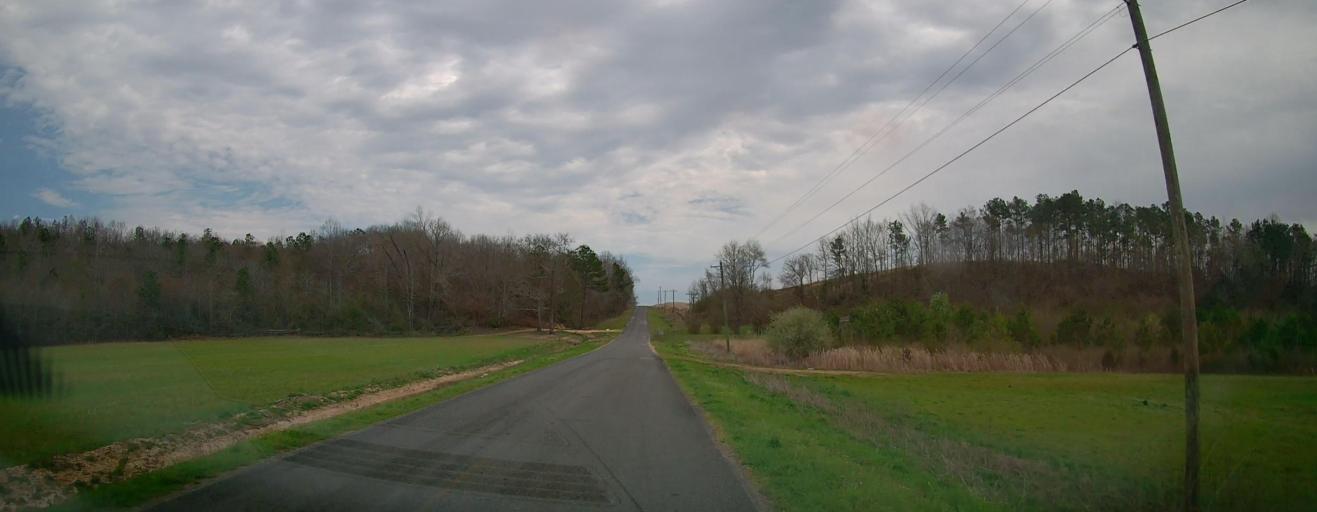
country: US
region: Alabama
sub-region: Marion County
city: Hamilton
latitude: 34.1852
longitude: -88.1376
